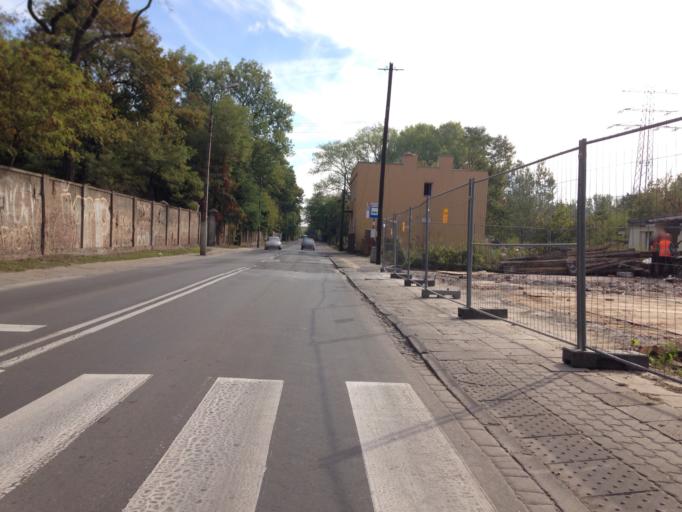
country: PL
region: Masovian Voivodeship
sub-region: Warszawa
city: Praga Poludnie
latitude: 52.2620
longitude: 21.0643
